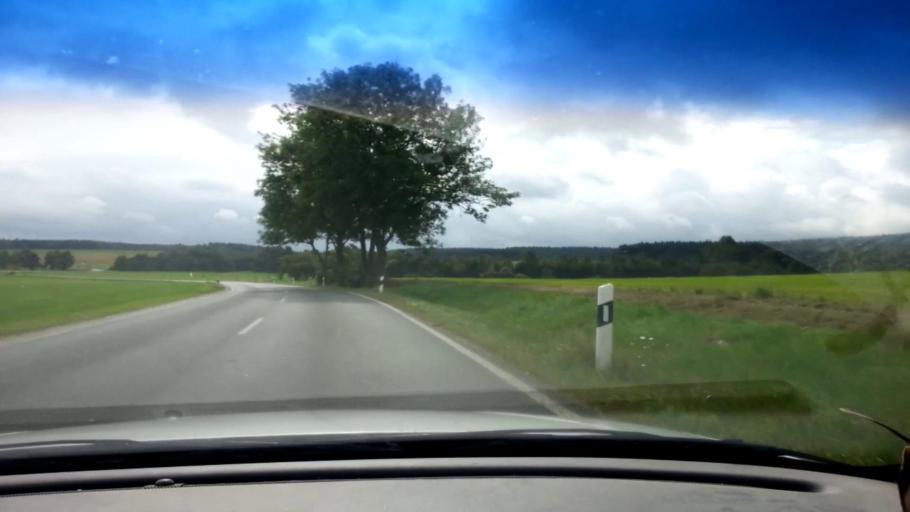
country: DE
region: Bavaria
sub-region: Upper Franconia
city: Weissenstadt
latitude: 50.0950
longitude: 11.8926
